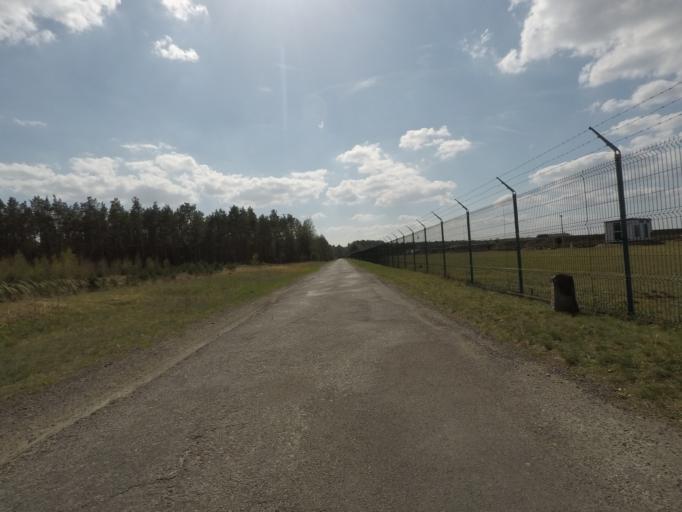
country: DE
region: Brandenburg
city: Melchow
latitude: 52.8237
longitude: 13.7157
